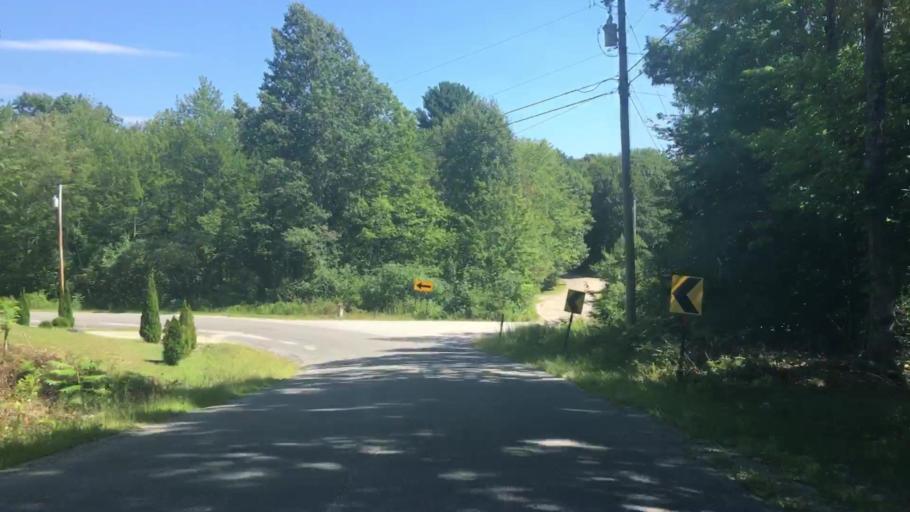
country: US
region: Maine
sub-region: Androscoggin County
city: Sabattus
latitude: 44.1176
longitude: -70.0266
